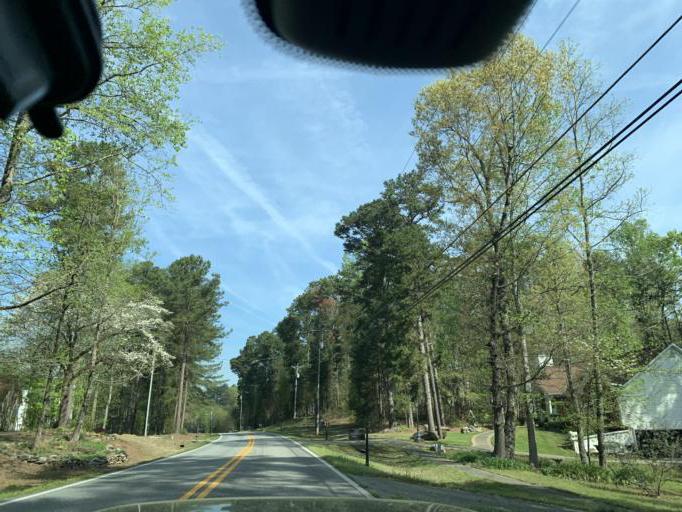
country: US
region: Georgia
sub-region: Forsyth County
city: Cumming
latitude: 34.2107
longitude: -84.0739
